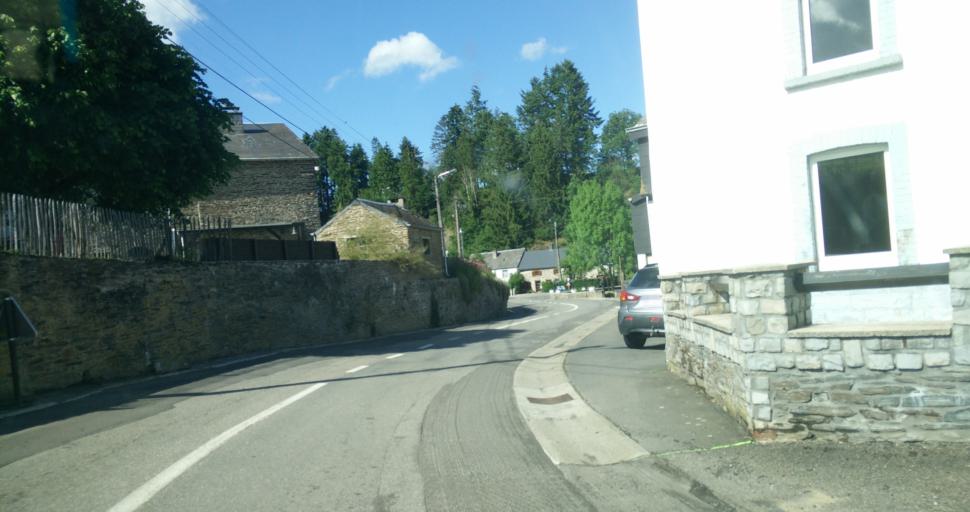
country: BE
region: Wallonia
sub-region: Province du Luxembourg
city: Bertogne
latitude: 50.1616
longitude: 5.6850
